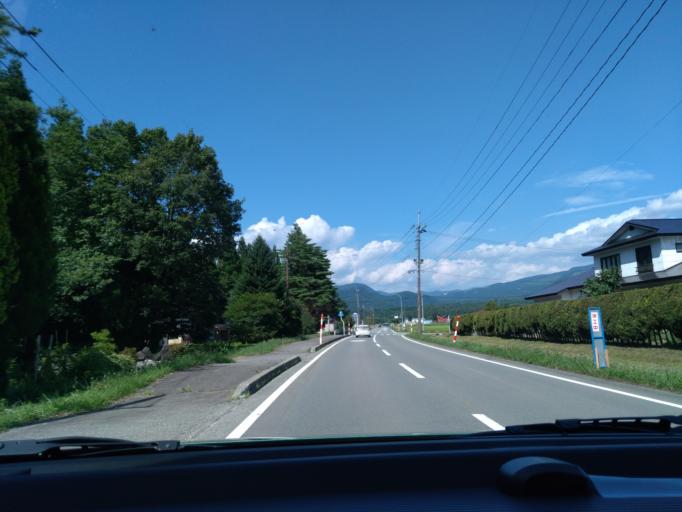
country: JP
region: Akita
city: Kakunodatemachi
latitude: 39.7366
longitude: 140.7086
